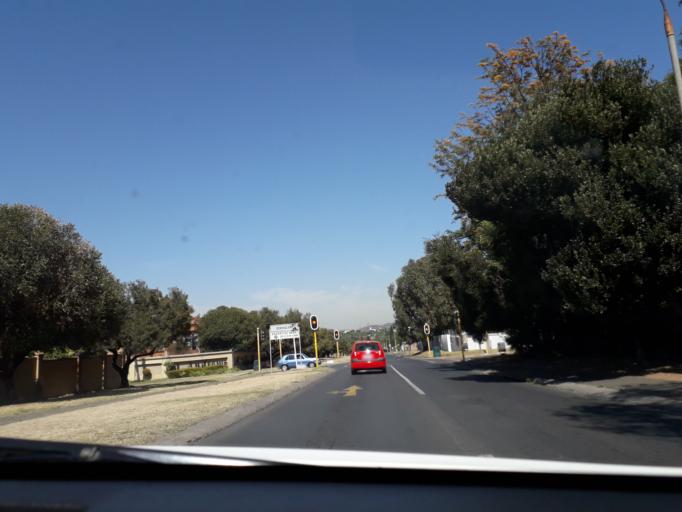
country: ZA
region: Gauteng
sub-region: City of Johannesburg Metropolitan Municipality
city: Modderfontein
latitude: -26.1384
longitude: 28.1748
